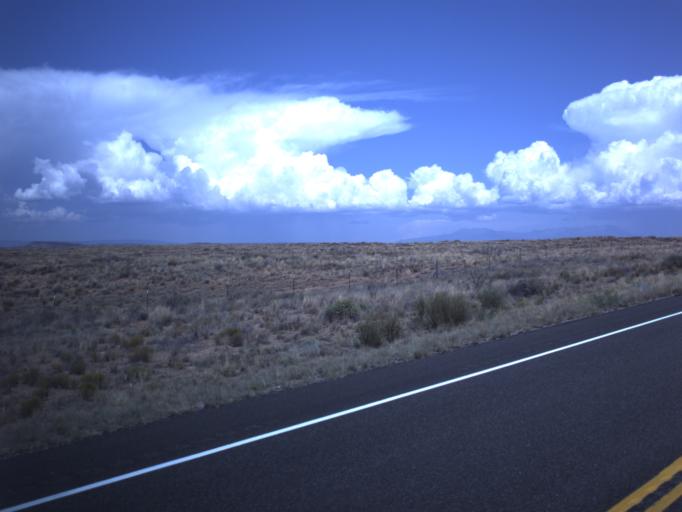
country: US
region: Utah
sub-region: San Juan County
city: Blanding
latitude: 37.3038
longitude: -109.5303
